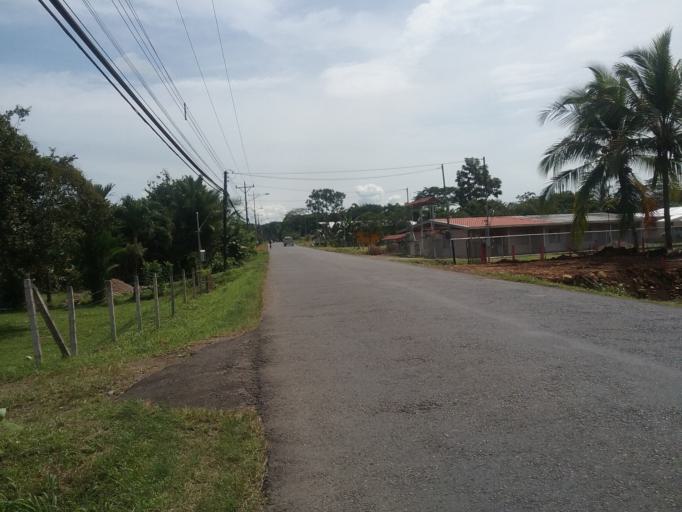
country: CR
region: Limon
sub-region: Canton de Pococi
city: Guapiles
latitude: 10.3204
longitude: -83.8996
